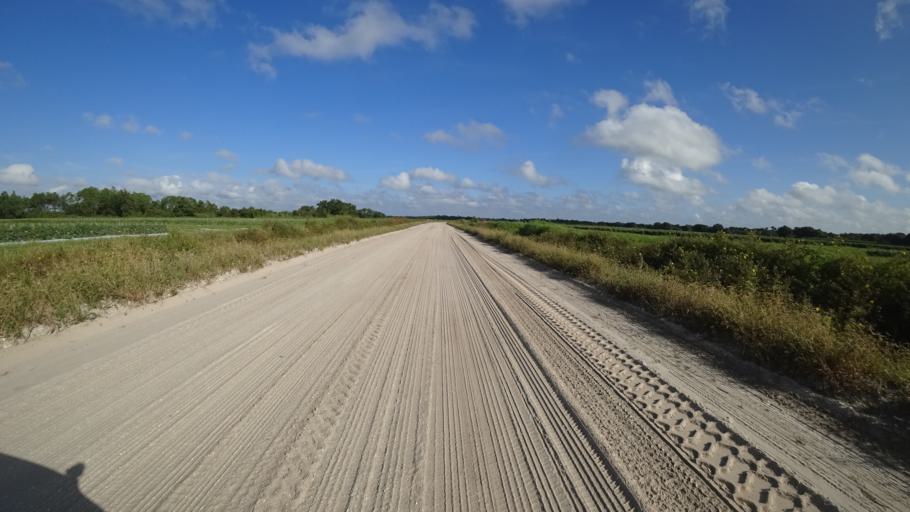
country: US
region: Florida
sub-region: Hillsborough County
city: Wimauma
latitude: 27.5473
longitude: -82.3209
